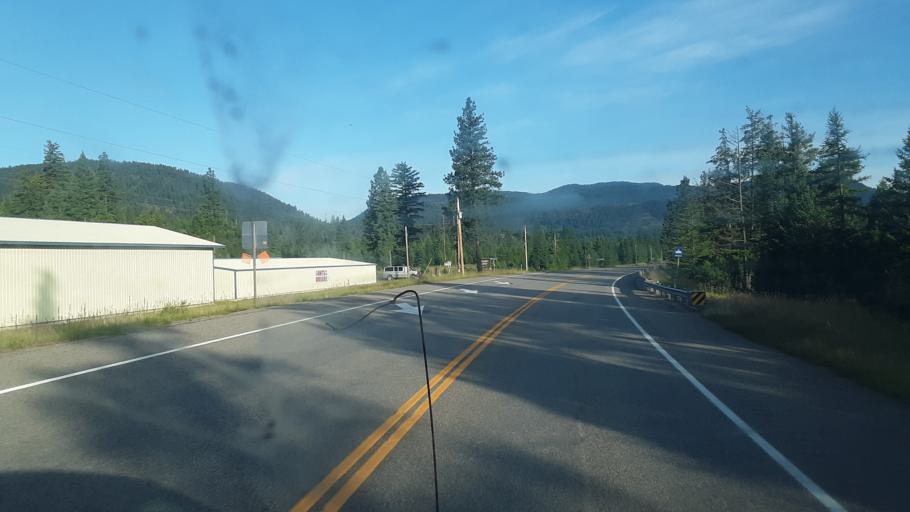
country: US
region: Montana
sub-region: Lincoln County
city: Libby
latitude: 48.4375
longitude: -115.8608
